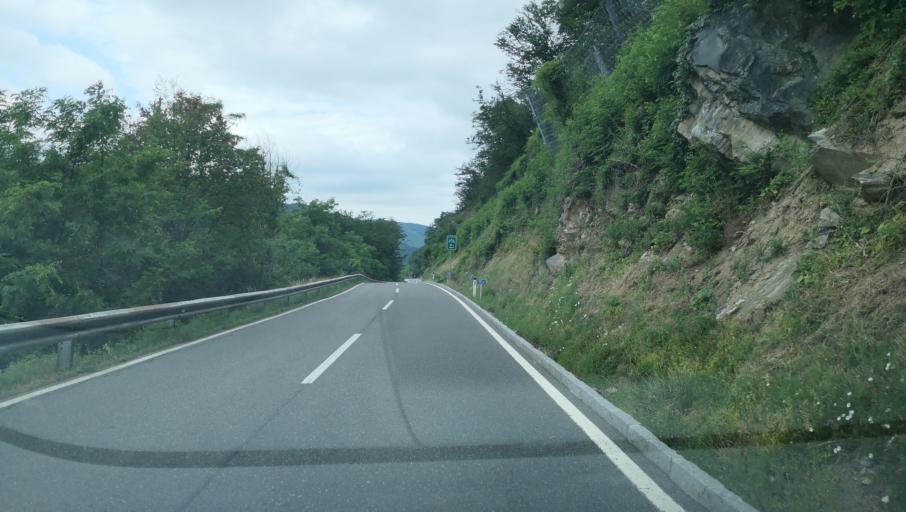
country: AT
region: Lower Austria
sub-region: Politischer Bezirk Krems
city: Aggsbach
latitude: 48.3207
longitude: 15.4132
